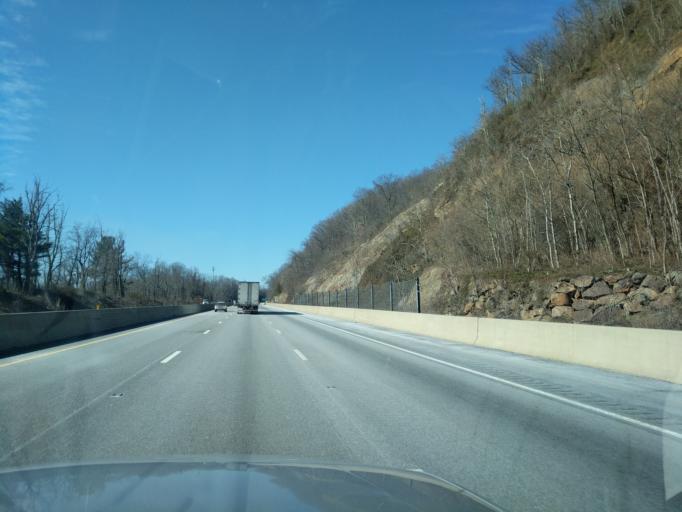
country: US
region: North Carolina
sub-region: Haywood County
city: Canton
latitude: 35.5402
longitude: -82.7830
